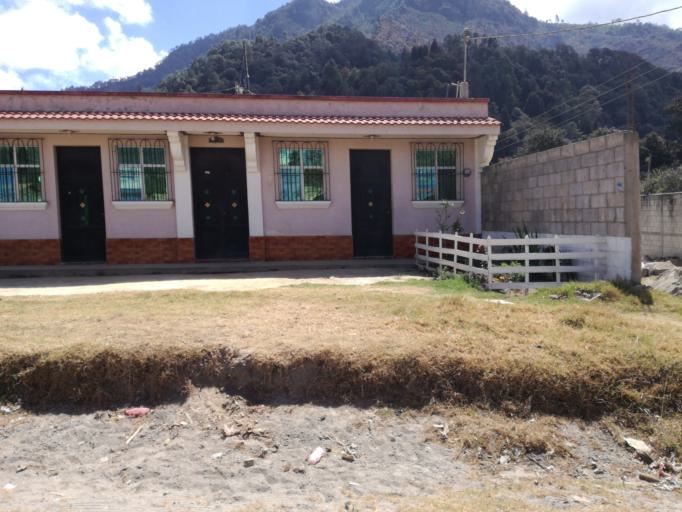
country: GT
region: Quetzaltenango
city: Almolonga
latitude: 14.7967
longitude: -91.5374
